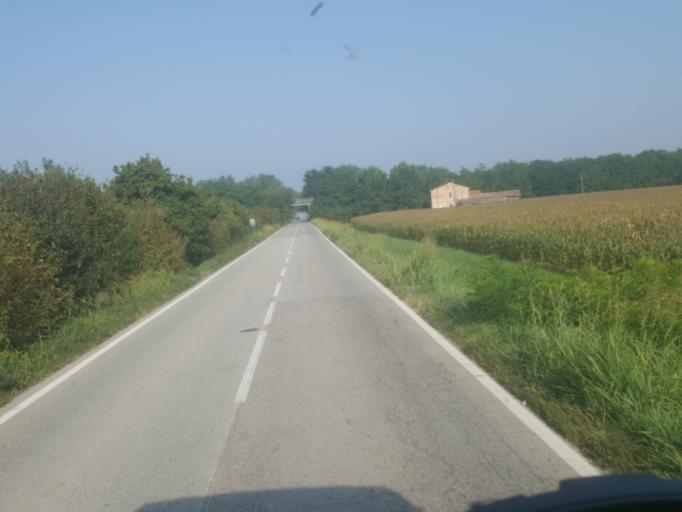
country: IT
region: Emilia-Romagna
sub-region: Provincia di Ravenna
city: Lavezzola
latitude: 44.5729
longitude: 11.8825
